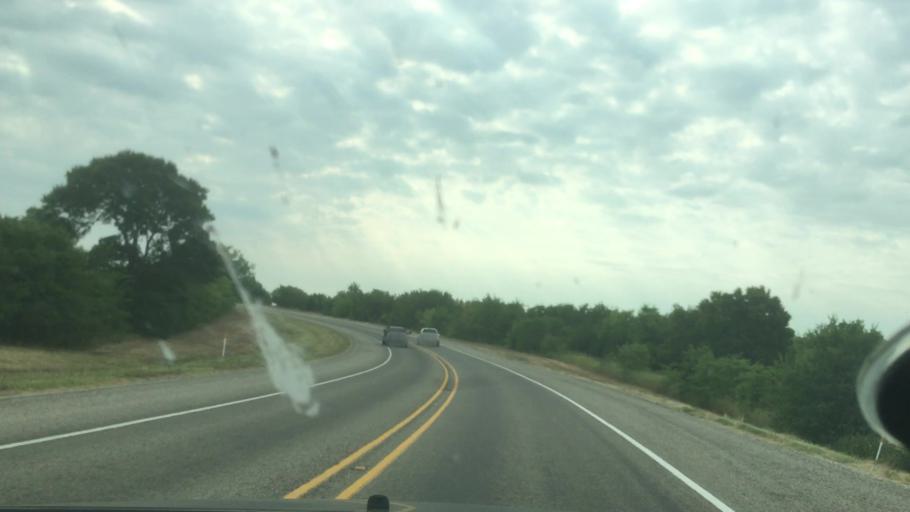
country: US
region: Texas
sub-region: Grayson County
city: Pottsboro
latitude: 33.8000
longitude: -96.6512
